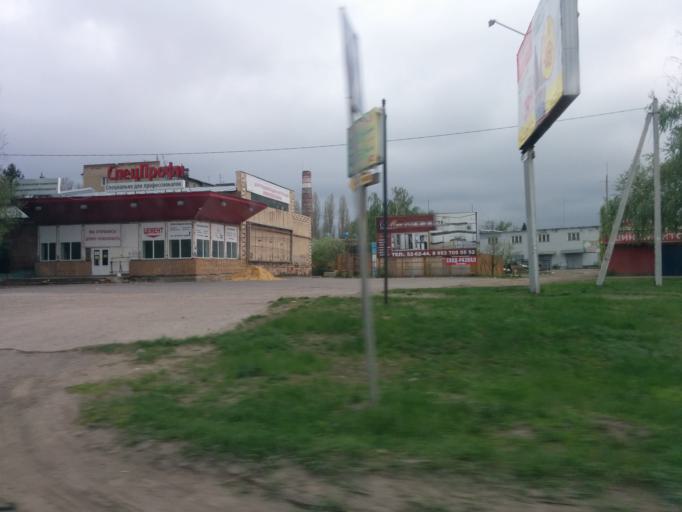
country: RU
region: Tambov
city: Tambov
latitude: 52.7274
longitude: 41.4354
